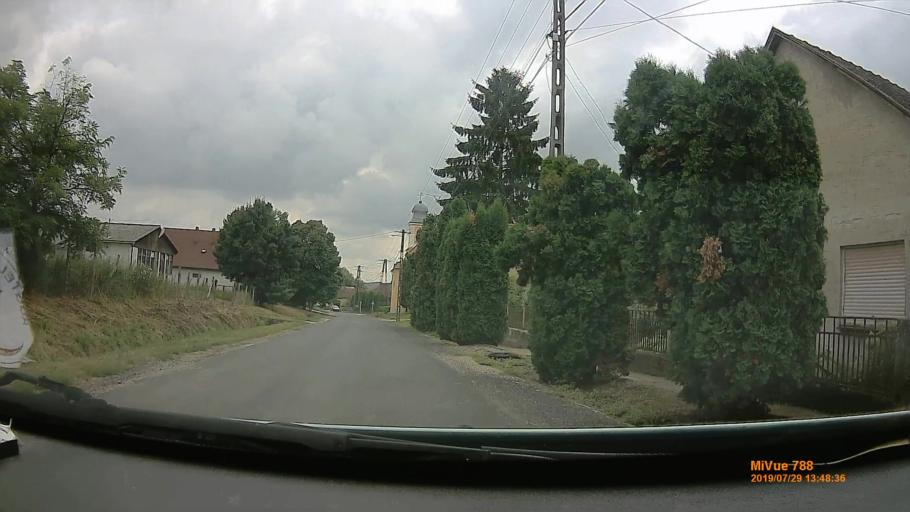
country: HU
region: Somogy
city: Tab
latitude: 46.7834
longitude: 17.9513
